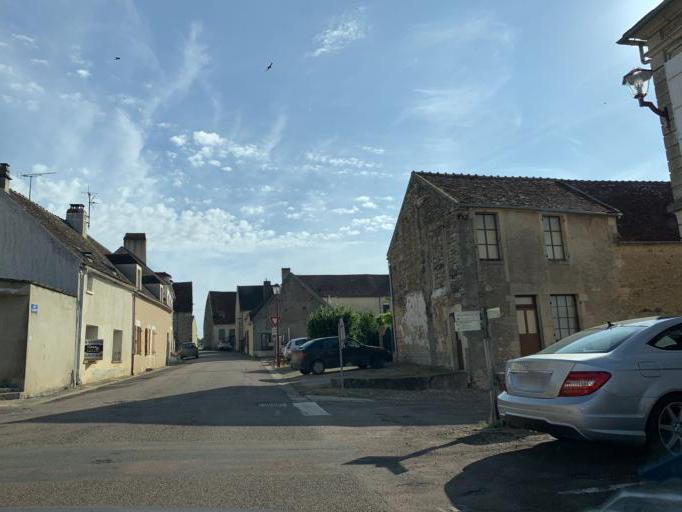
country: FR
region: Bourgogne
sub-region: Departement de la Nievre
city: Varzy
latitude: 47.4470
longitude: 3.4142
